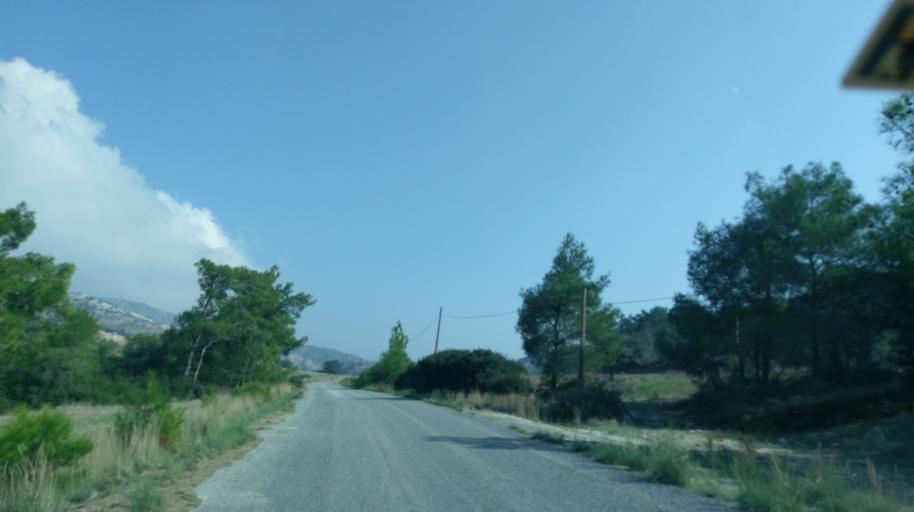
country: CY
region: Ammochostos
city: Lefkonoiko
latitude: 35.3160
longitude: 33.6444
